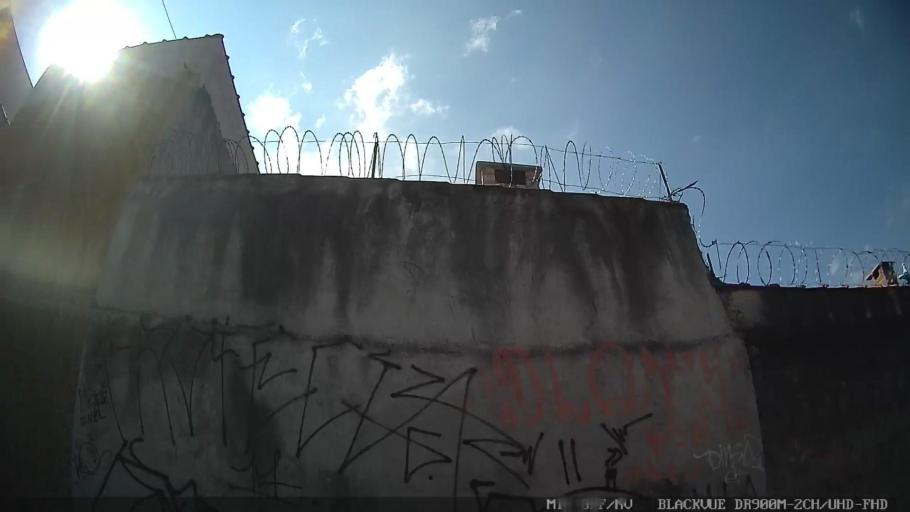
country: BR
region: Sao Paulo
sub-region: Ferraz De Vasconcelos
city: Ferraz de Vasconcelos
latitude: -23.5195
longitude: -46.4289
